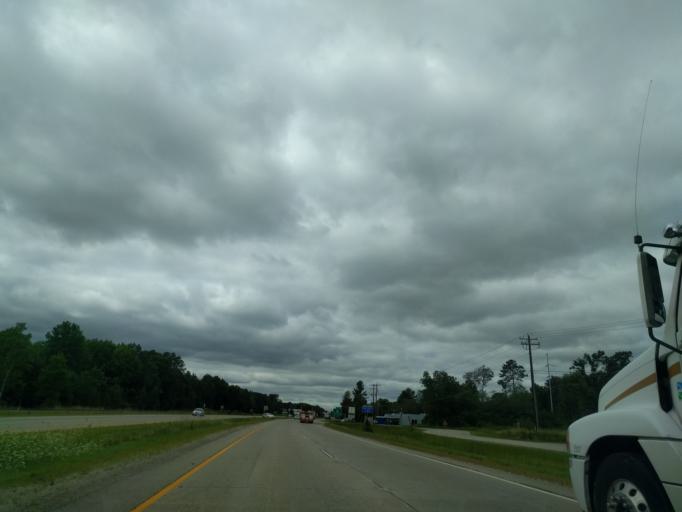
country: US
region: Wisconsin
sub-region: Marinette County
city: Marinette
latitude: 45.0702
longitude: -87.6826
